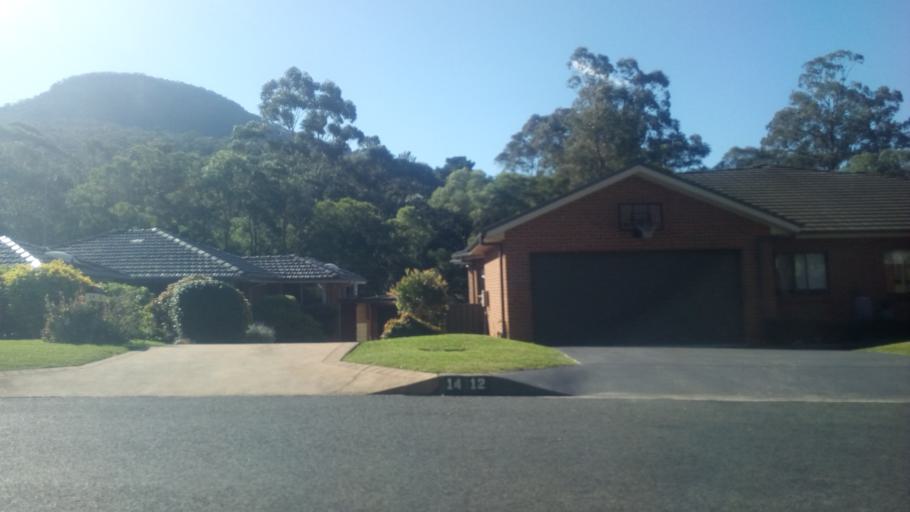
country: AU
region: New South Wales
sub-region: Wollongong
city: Mount Keira
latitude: -34.4177
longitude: 150.8541
